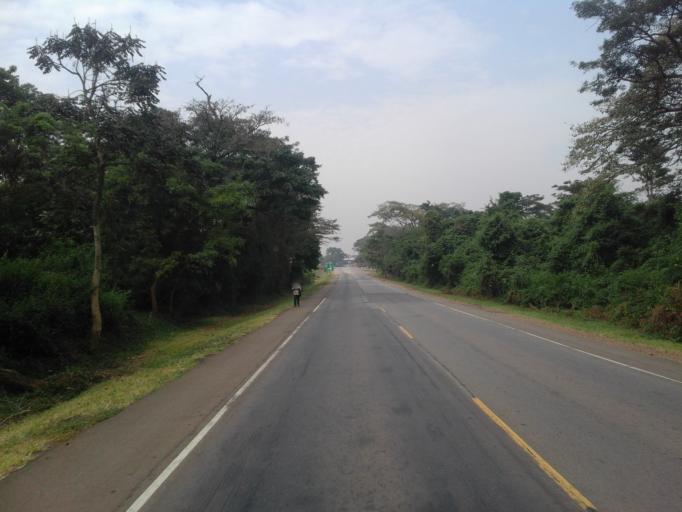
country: UG
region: Eastern Region
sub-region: Busia District
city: Busia
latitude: 0.5261
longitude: 33.9706
